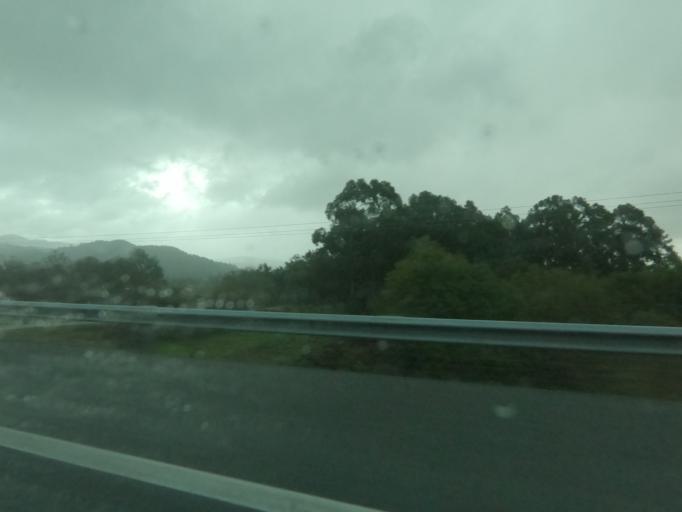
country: ES
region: Galicia
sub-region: Provincia de Pontevedra
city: Marin
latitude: 42.3572
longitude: -8.6411
